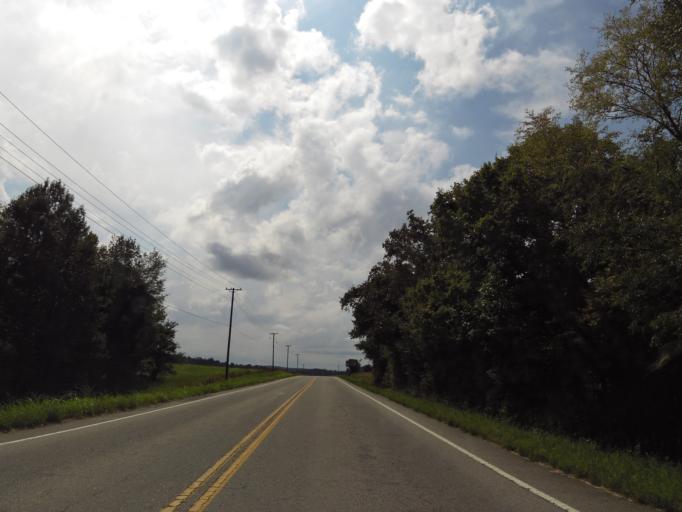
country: US
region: Tennessee
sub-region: Perry County
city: Linden
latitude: 35.8286
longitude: -87.7868
